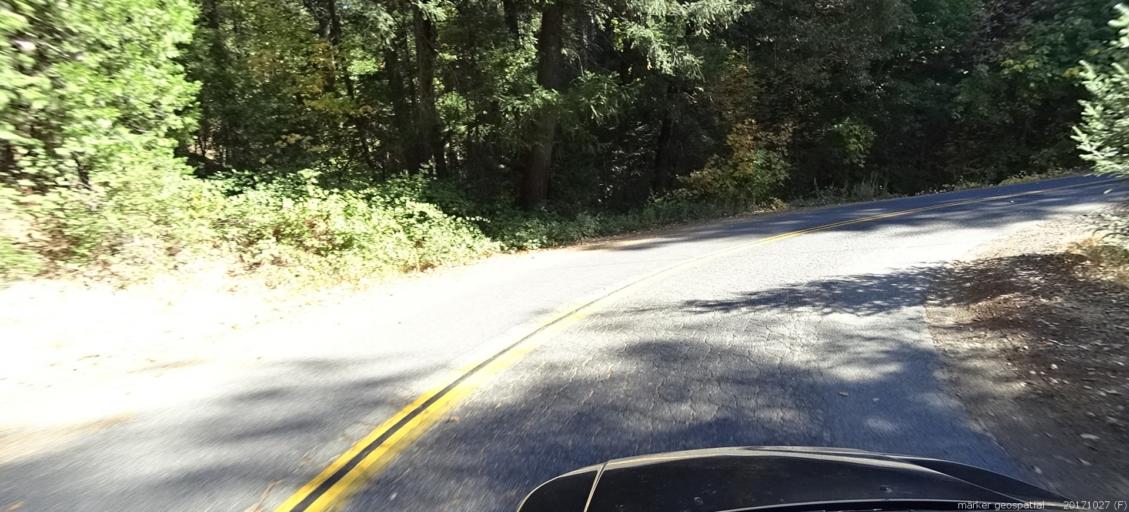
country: US
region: California
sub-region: Shasta County
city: Bella Vista
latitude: 40.8191
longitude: -121.9804
